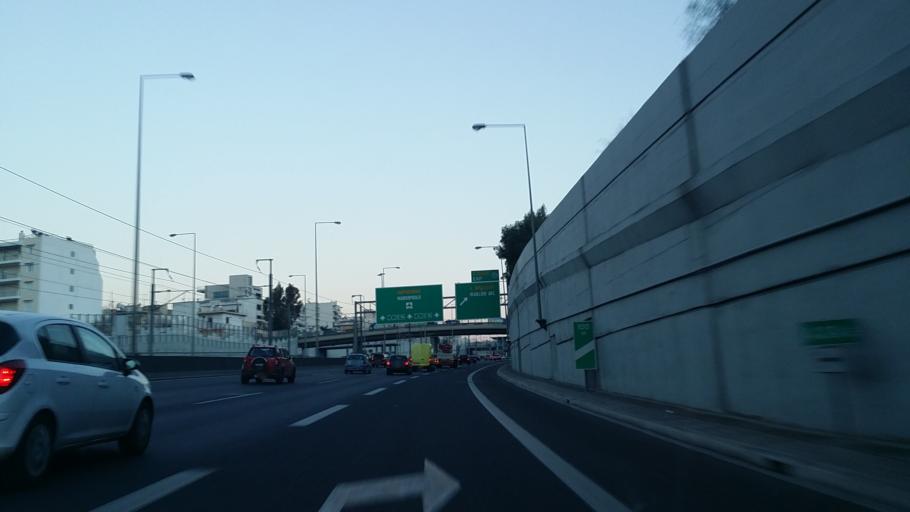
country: GR
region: Attica
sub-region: Nomarchia Athinas
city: Irakleio
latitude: 38.0592
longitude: 23.7654
